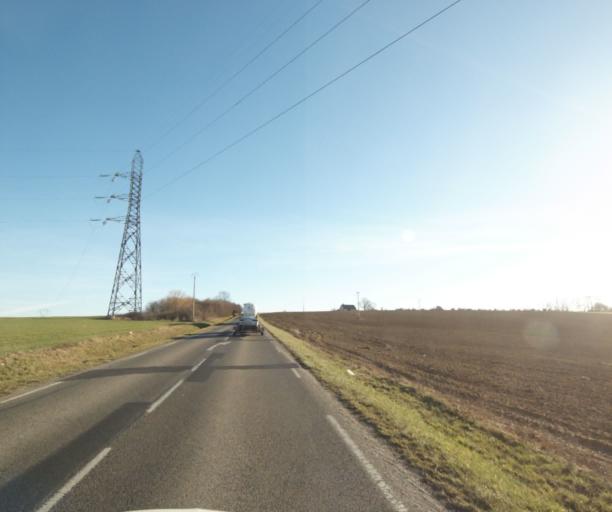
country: FR
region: Lorraine
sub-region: Departement de Meurthe-et-Moselle
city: Art-sur-Meurthe
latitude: 48.6358
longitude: 6.2543
